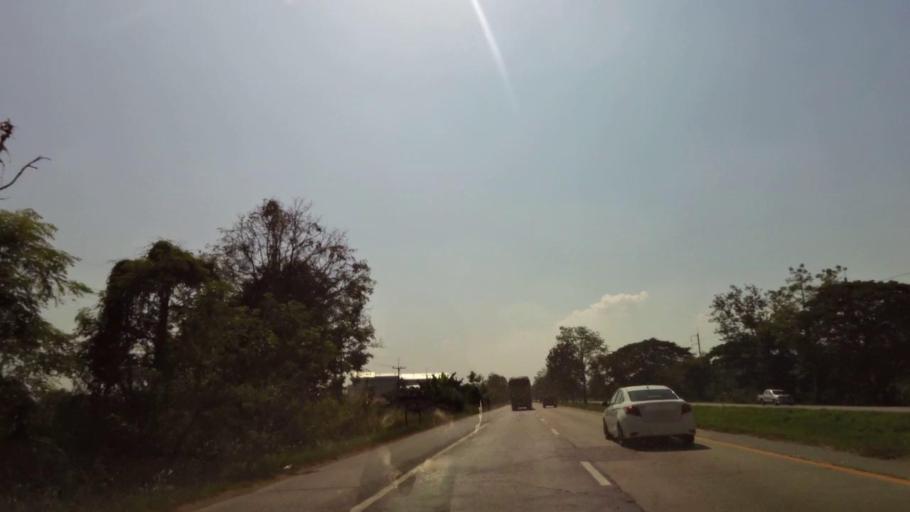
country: TH
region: Phichit
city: Wachira Barami
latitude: 16.6050
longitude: 100.1484
